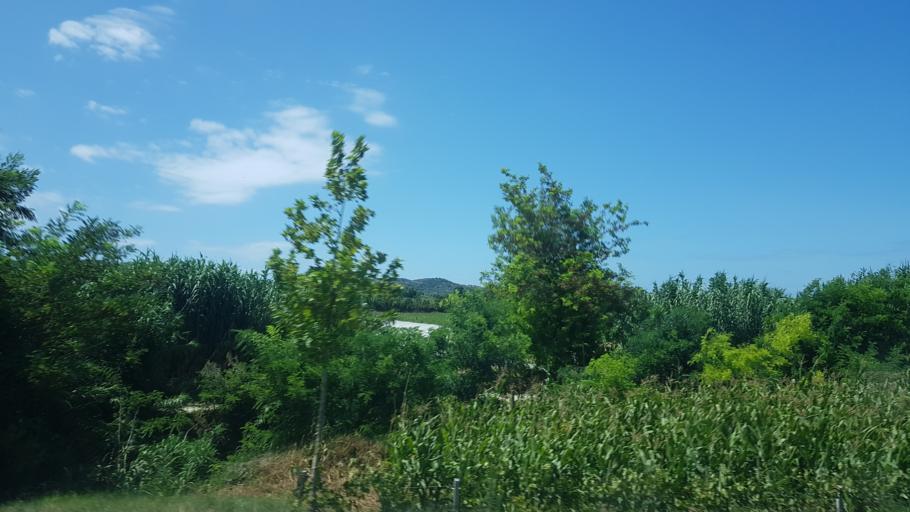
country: AL
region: Fier
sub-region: Rrethi i Fierit
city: Frakulla e Madhe
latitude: 40.6142
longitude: 19.5222
